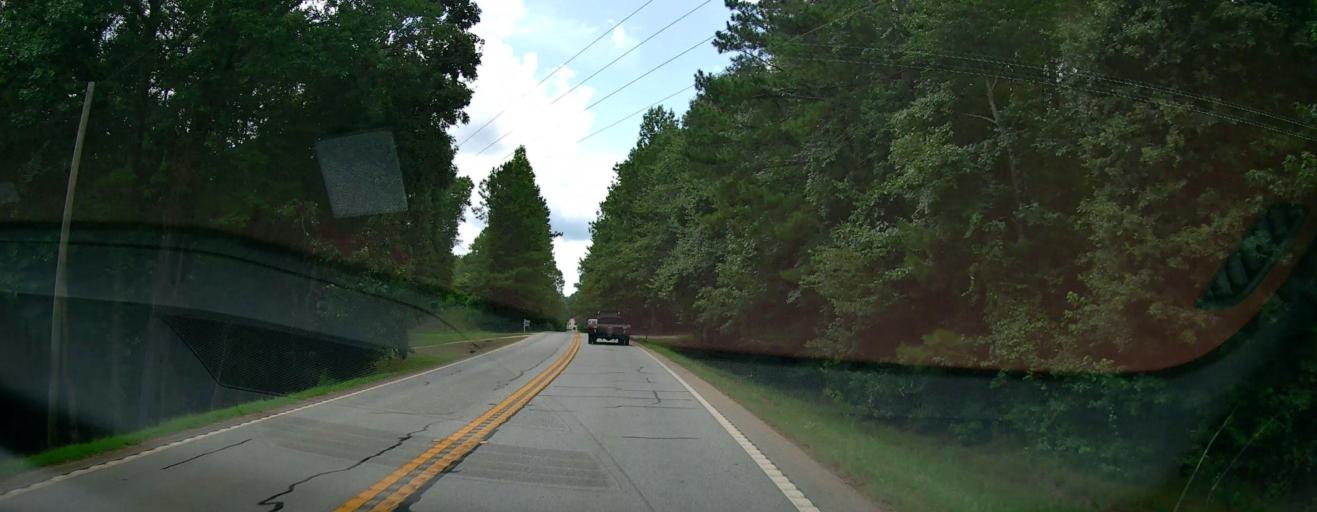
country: US
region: Georgia
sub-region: Heard County
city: Franklin
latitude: 33.2983
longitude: -85.1225
